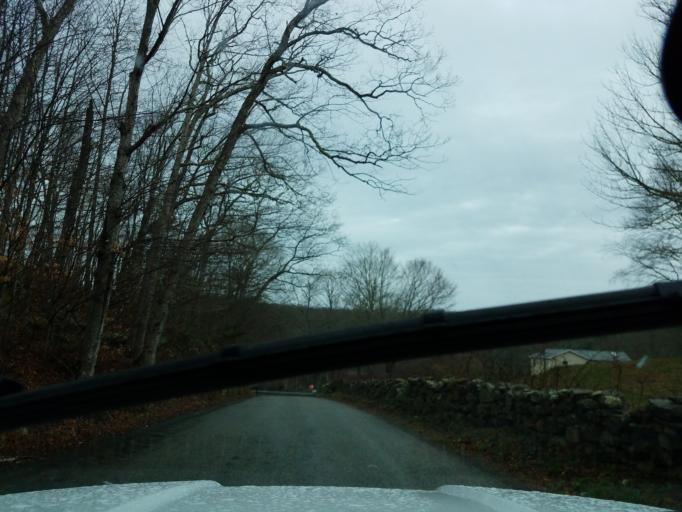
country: US
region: Rhode Island
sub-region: Washington County
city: Hopkinton
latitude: 41.4542
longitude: -71.8222
